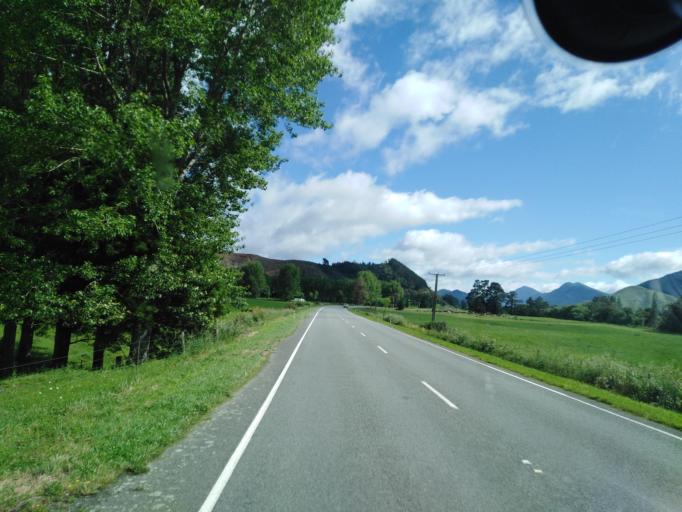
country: NZ
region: Nelson
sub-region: Nelson City
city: Nelson
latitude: -41.2697
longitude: 173.5726
